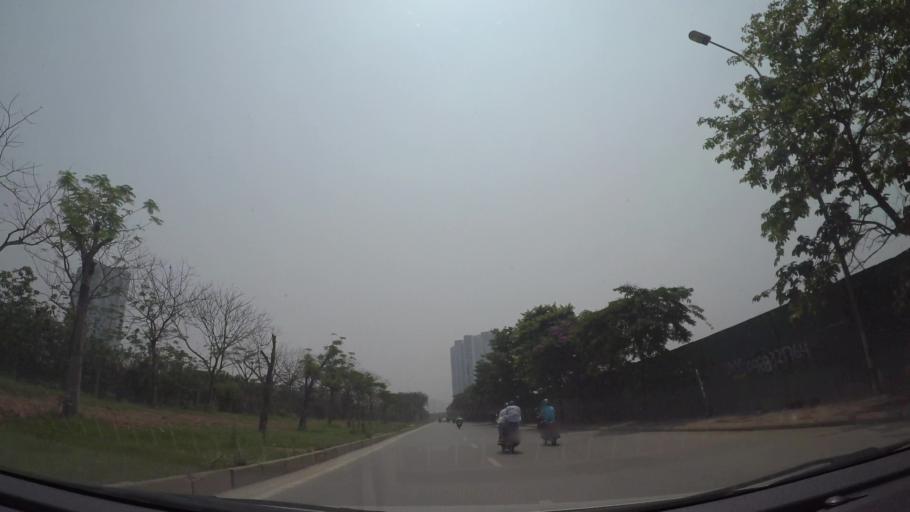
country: VN
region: Ha Noi
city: Thanh Xuan
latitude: 21.0029
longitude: 105.7770
